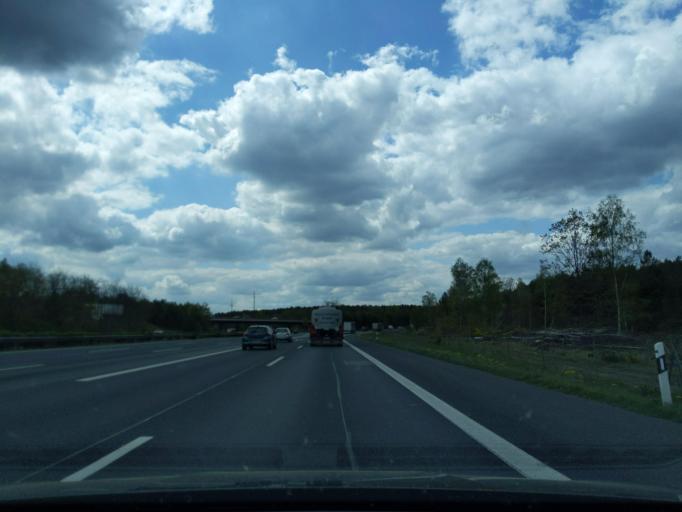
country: DE
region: Brandenburg
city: Fichtenwalde
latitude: 52.2919
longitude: 12.9227
